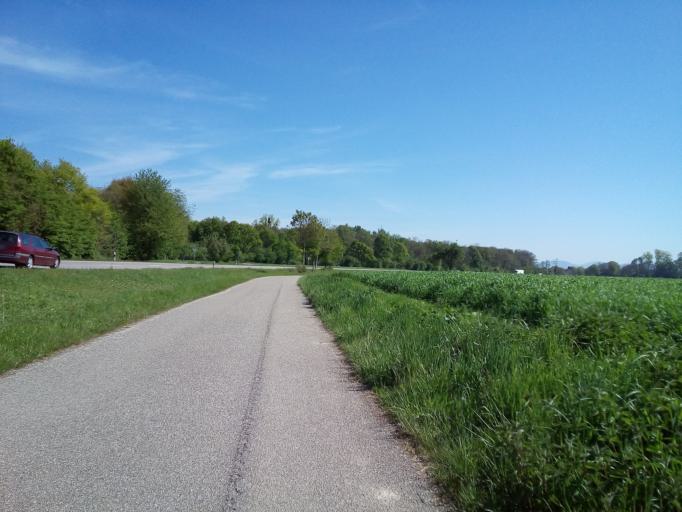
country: DE
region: Baden-Wuerttemberg
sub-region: Freiburg Region
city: Rheinau
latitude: 48.6786
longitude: 7.9639
